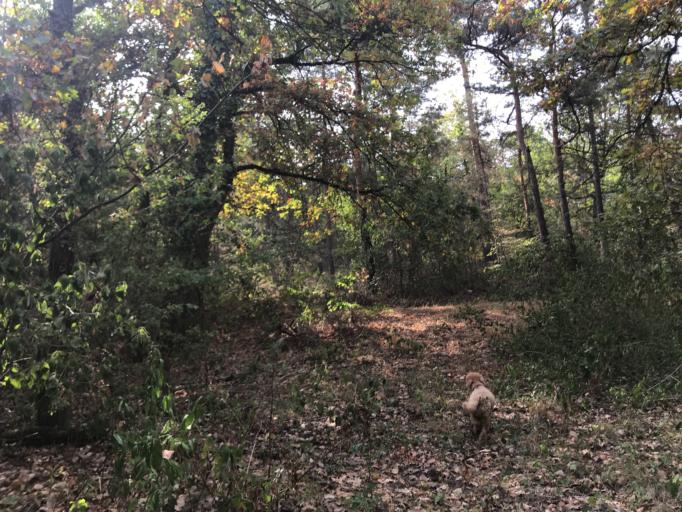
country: DE
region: Rheinland-Pfalz
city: Budenheim
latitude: 50.0051
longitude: 8.1521
